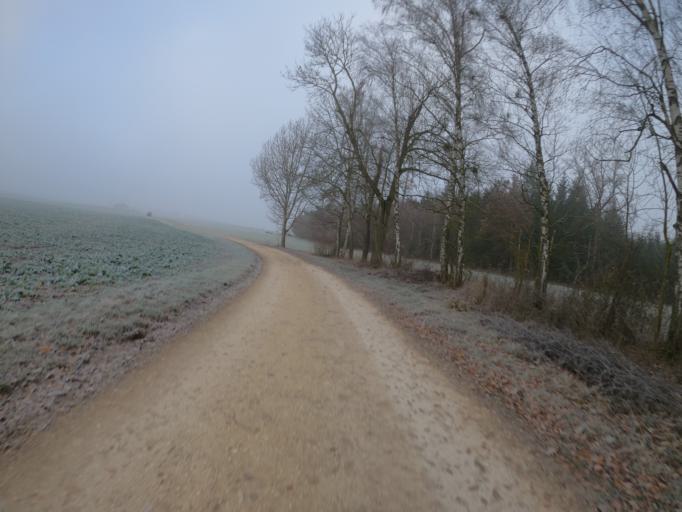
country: DE
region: Baden-Wuerttemberg
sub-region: Tuebingen Region
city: Beimerstetten
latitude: 48.4925
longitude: 9.9657
